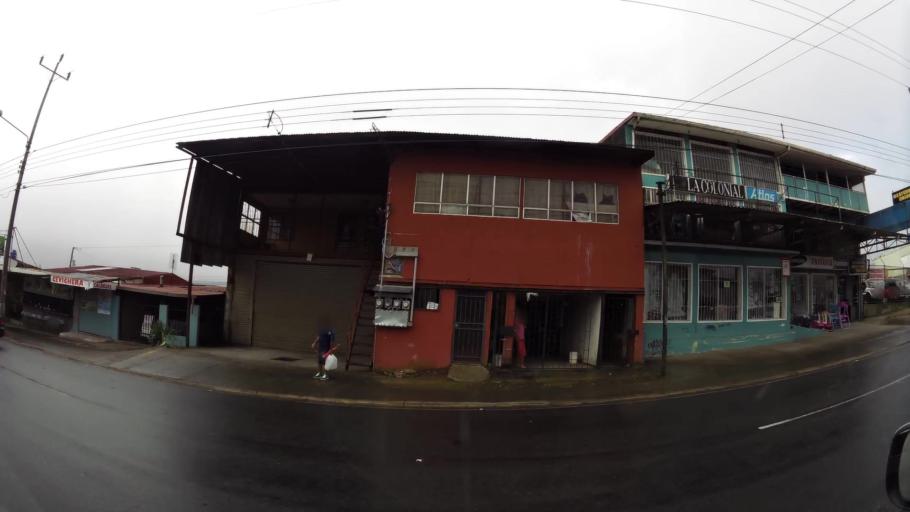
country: CR
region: Cartago
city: Paraiso
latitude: 9.8412
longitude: -83.8781
